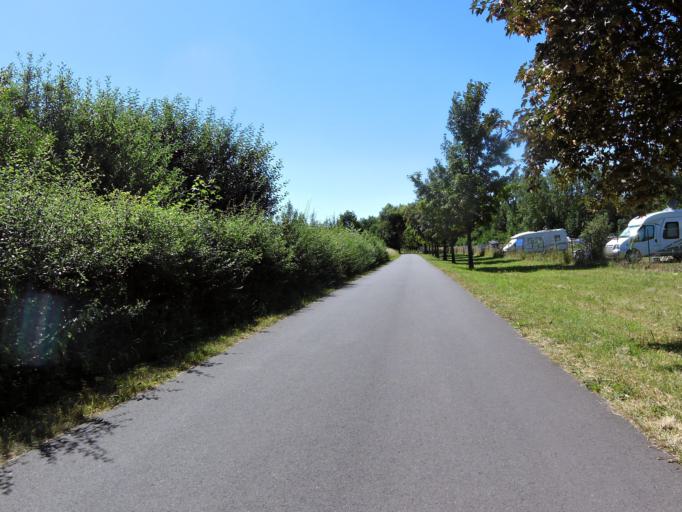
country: DE
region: Bavaria
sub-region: Regierungsbezirk Unterfranken
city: Eibelstadt
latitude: 49.7314
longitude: 9.9884
